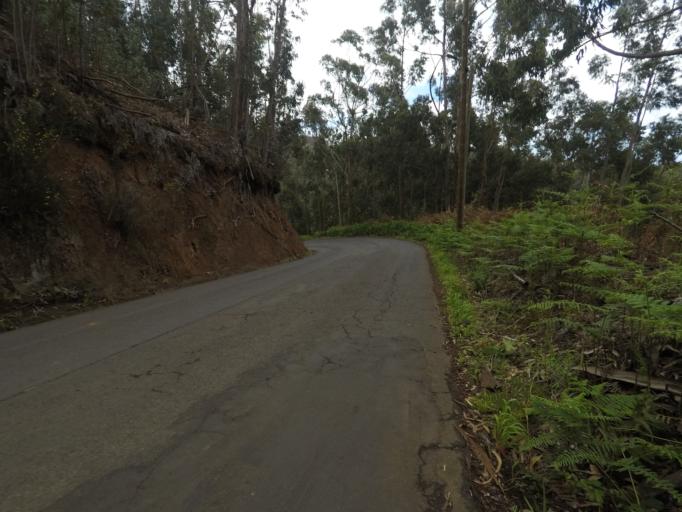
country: PT
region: Madeira
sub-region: Calheta
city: Estreito da Calheta
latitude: 32.7542
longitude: -17.1972
